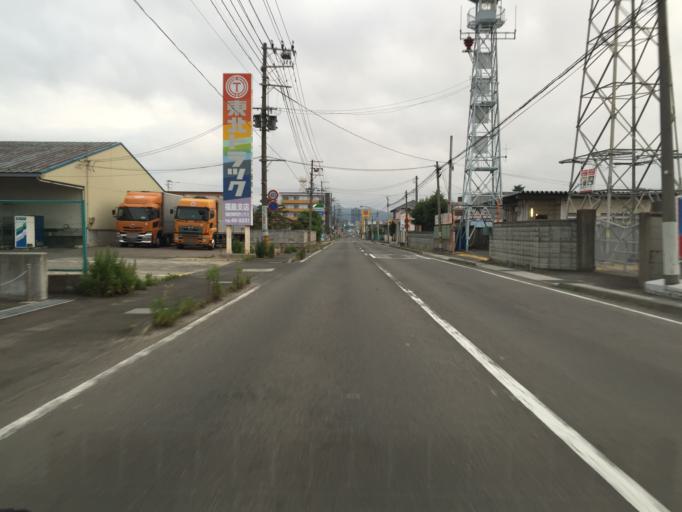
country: JP
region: Fukushima
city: Fukushima-shi
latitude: 37.7349
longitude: 140.4606
